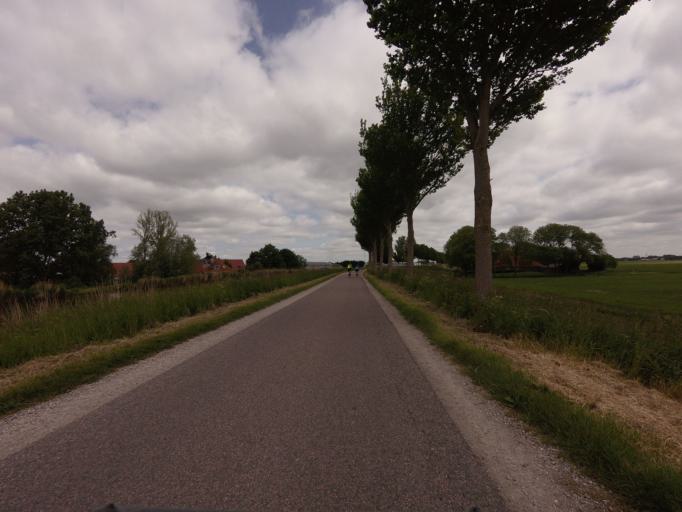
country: NL
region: North Holland
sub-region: Gemeente Beemster
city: Halfweg
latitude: 52.5462
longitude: 4.8440
